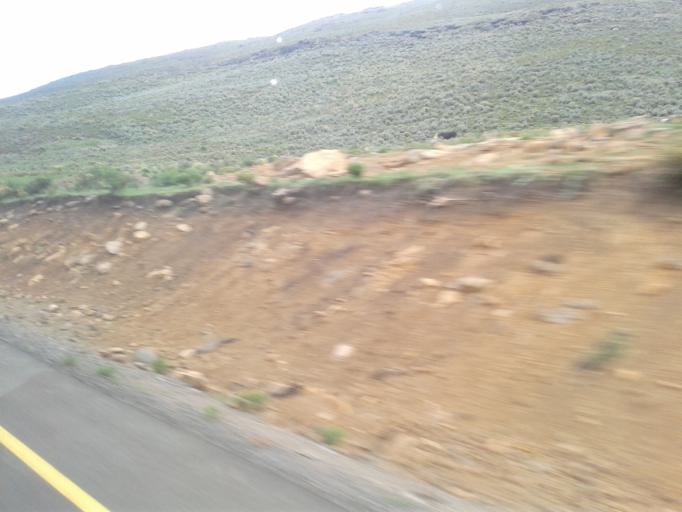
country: LS
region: Maseru
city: Nako
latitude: -29.7658
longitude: 28.0016
